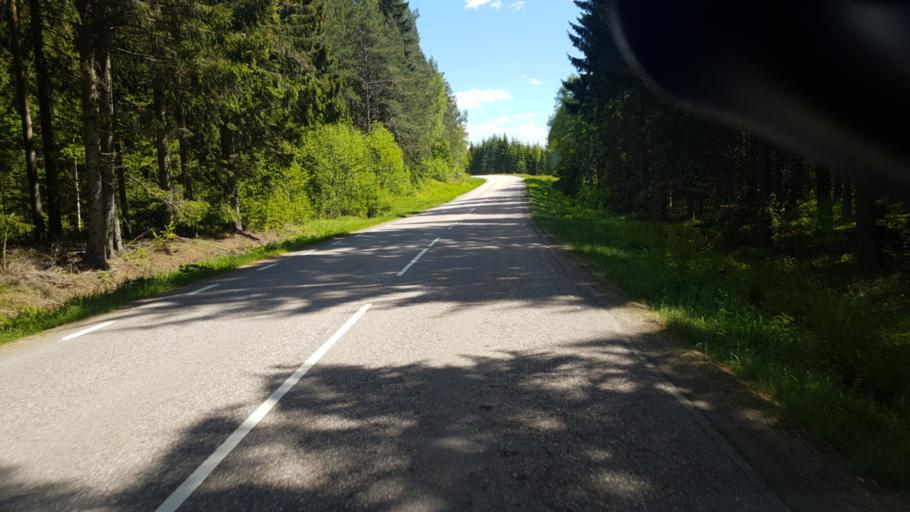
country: SE
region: Vaermland
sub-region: Arvika Kommun
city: Arvika
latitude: 59.6258
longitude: 12.8719
